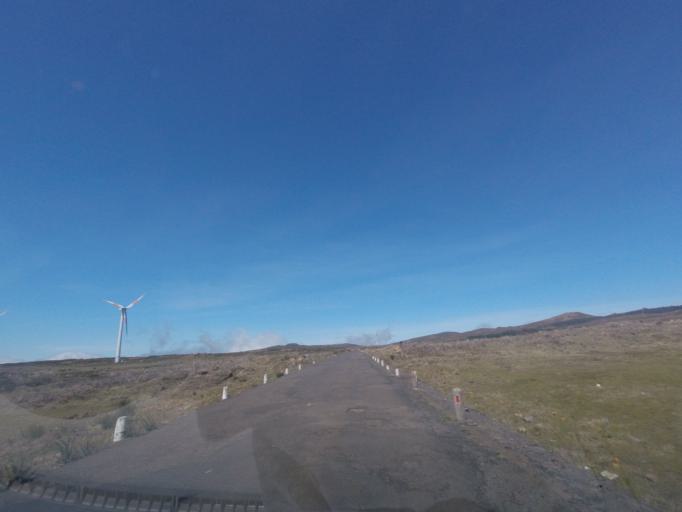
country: PT
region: Madeira
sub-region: Calheta
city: Arco da Calheta
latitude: 32.7430
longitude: -17.0972
